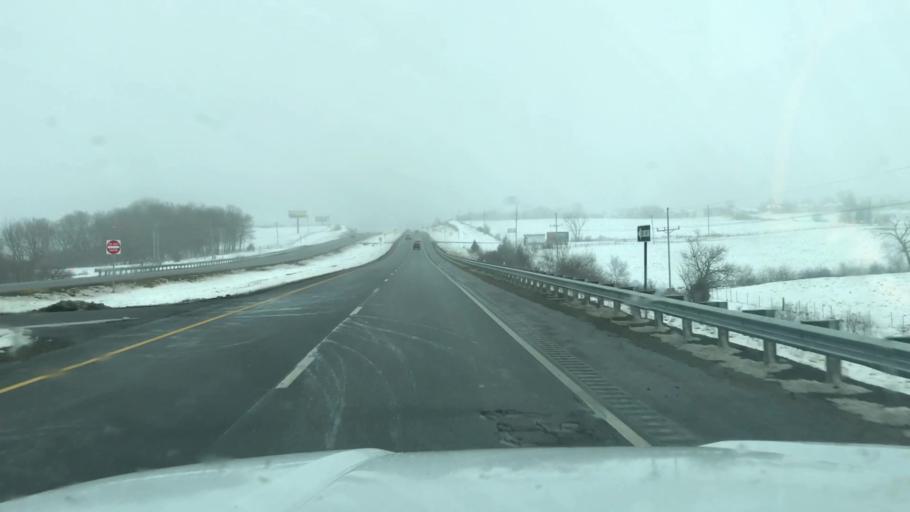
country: US
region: Missouri
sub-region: Clinton County
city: Cameron
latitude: 39.7539
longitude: -94.2659
